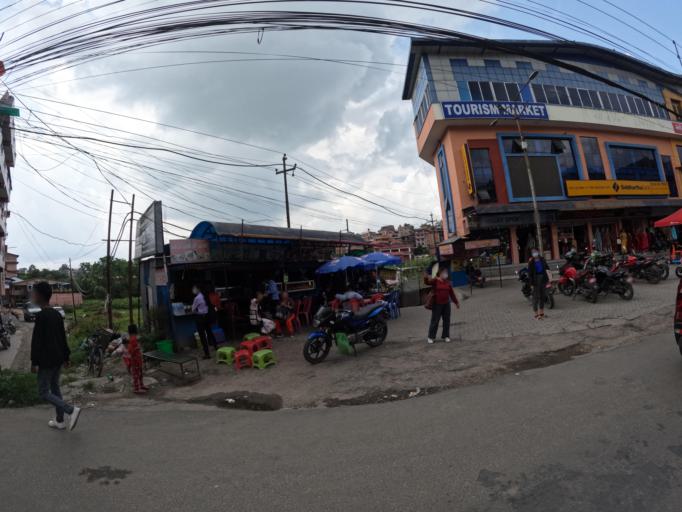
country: NP
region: Central Region
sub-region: Bagmati Zone
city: Bhaktapur
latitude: 27.6675
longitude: 85.4264
